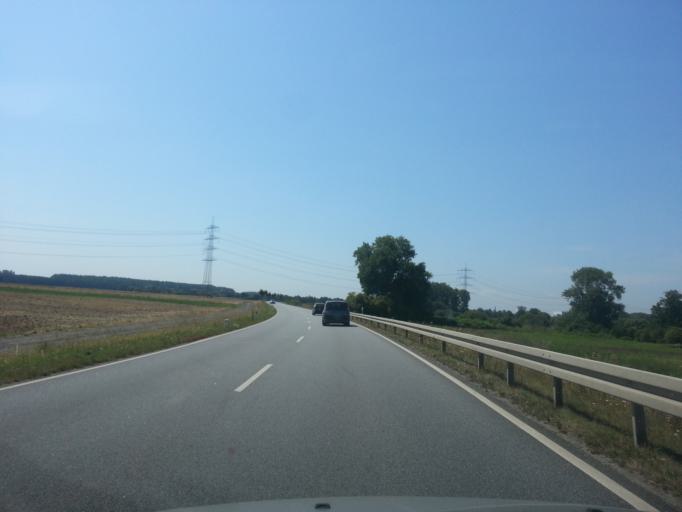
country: DE
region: Hesse
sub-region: Regierungsbezirk Darmstadt
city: Gross-Rohrheim
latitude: 49.7048
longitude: 8.4753
